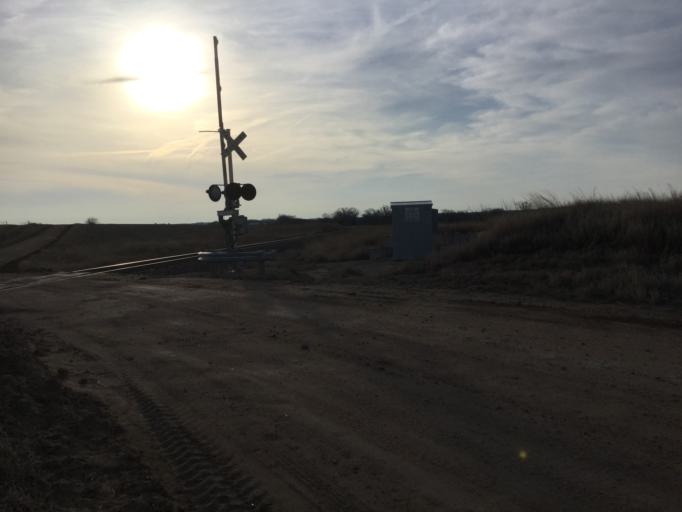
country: US
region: Kansas
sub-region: Ellis County
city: Ellis
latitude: 38.9431
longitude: -99.6309
